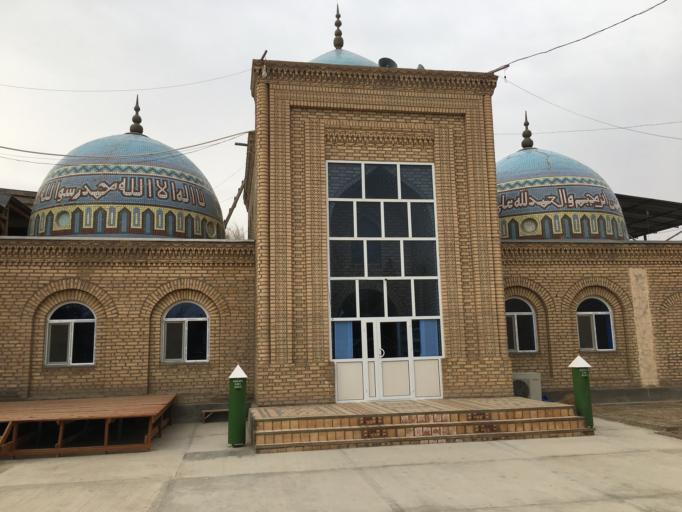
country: TM
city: Akdepe
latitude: 42.0454
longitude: 59.3827
